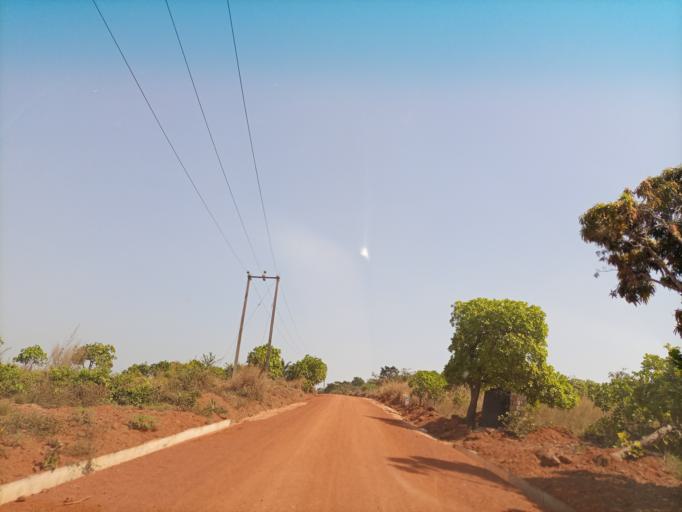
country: NG
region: Enugu
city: Nsukka
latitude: 6.7999
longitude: 7.3431
